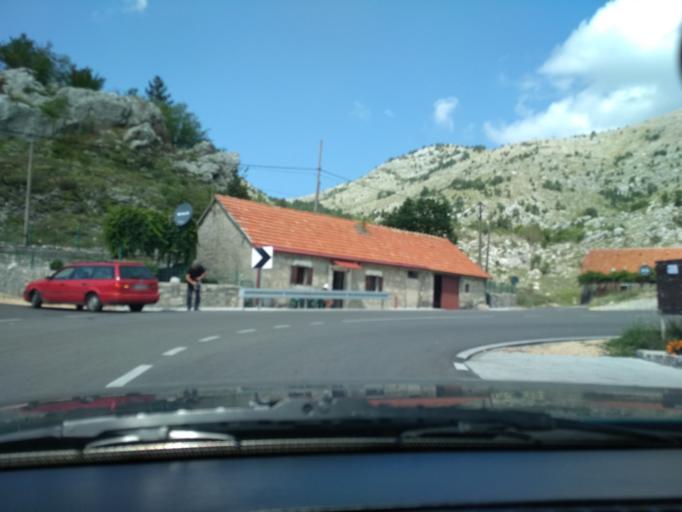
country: ME
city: Dobrota
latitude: 42.4377
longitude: 18.8289
